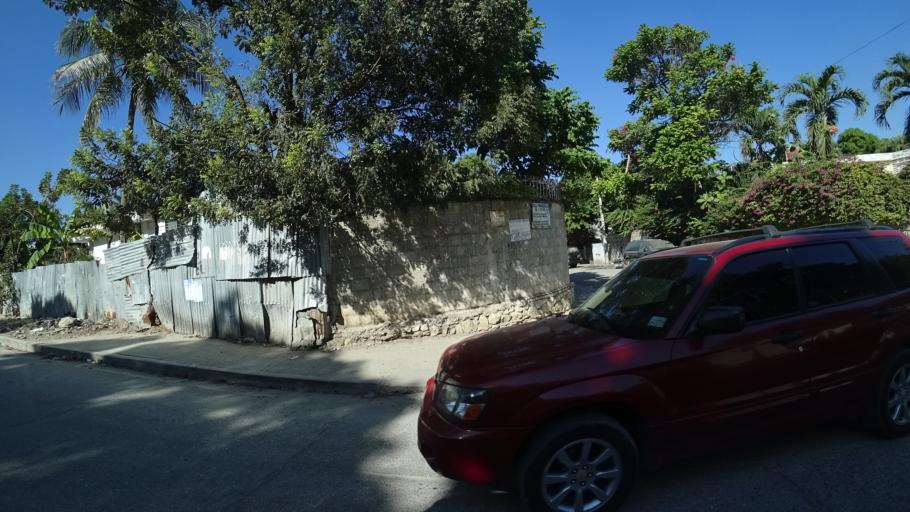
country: HT
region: Ouest
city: Delmas 73
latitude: 18.5562
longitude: -72.3070
